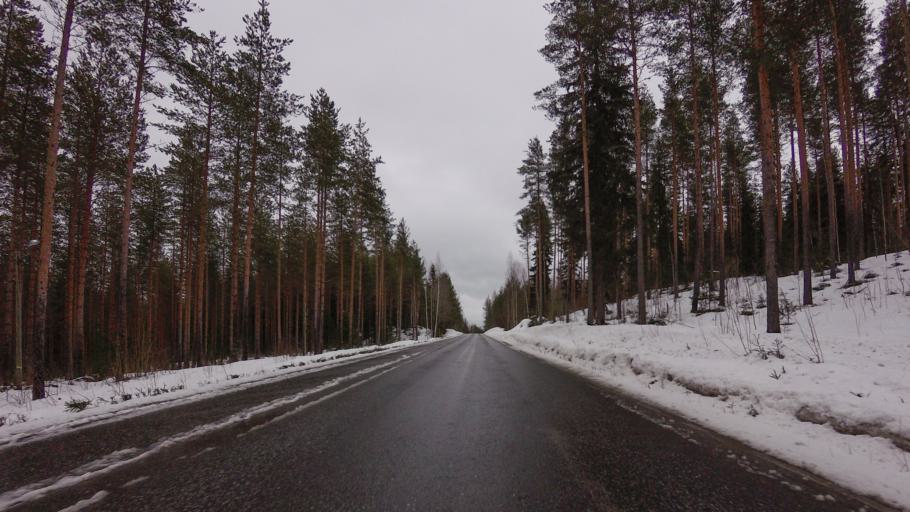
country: FI
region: Southern Savonia
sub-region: Savonlinna
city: Savonlinna
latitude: 61.9851
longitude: 28.7972
